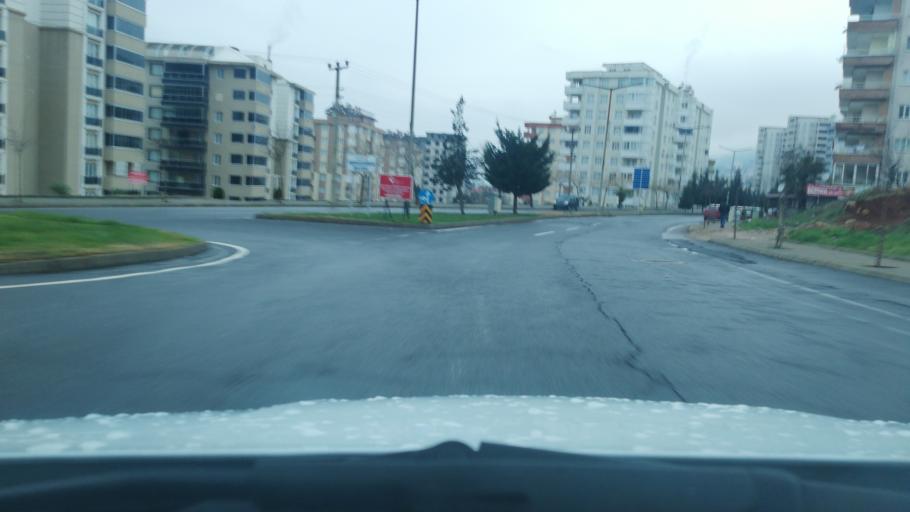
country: TR
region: Kahramanmaras
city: Kahramanmaras
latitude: 37.5910
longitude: 36.8772
